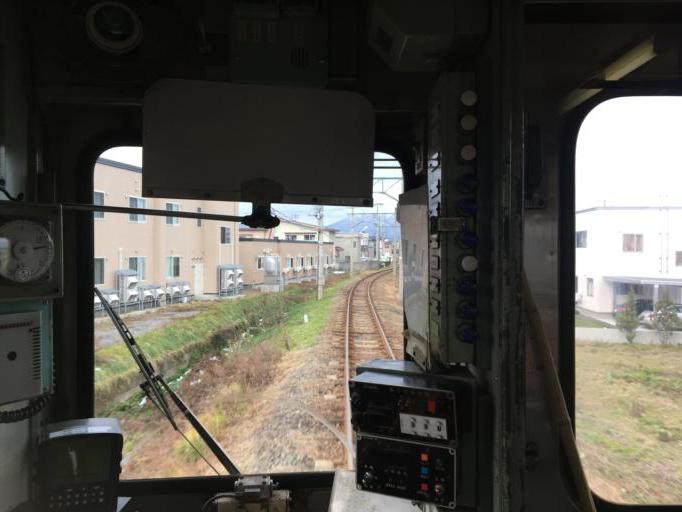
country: JP
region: Aomori
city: Hirosaki
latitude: 40.5661
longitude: 140.4824
